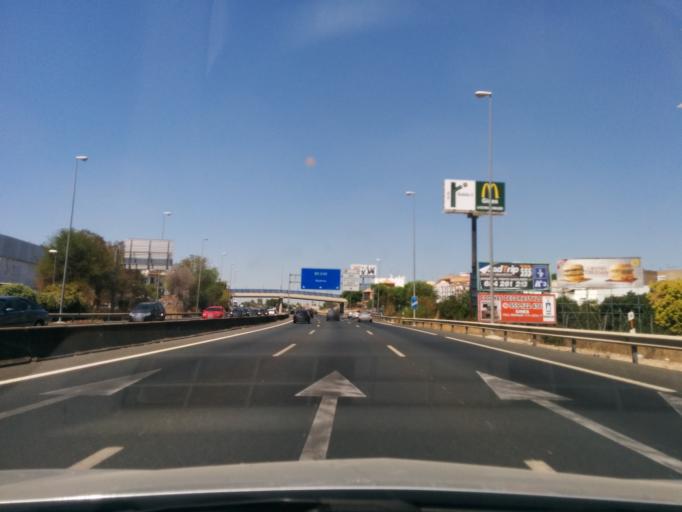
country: ES
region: Andalusia
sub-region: Provincia de Sevilla
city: Castilleja de la Cuesta
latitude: 37.3837
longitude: -6.0545
